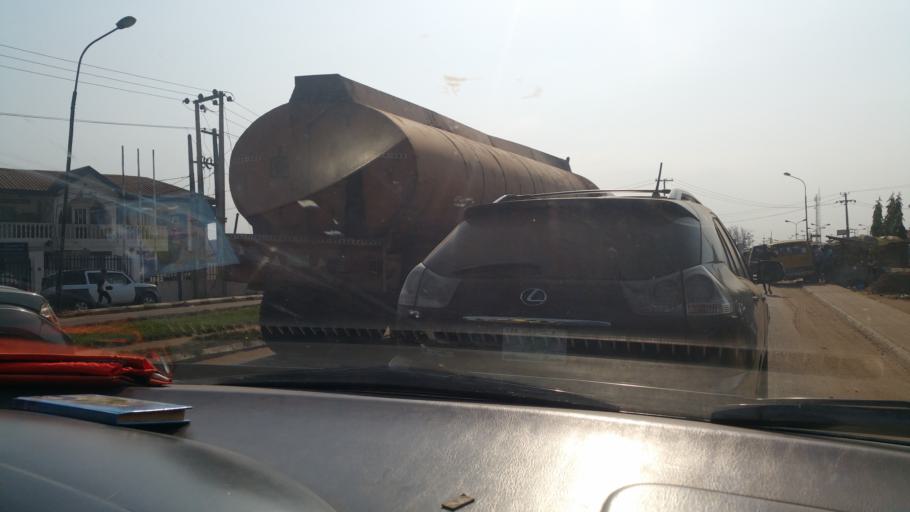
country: NG
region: Lagos
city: Ikotun
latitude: 6.5521
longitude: 3.2426
